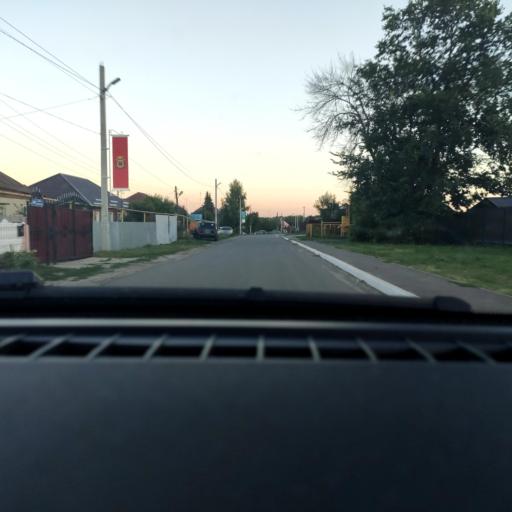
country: RU
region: Voronezj
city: Novaya Usman'
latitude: 51.6629
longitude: 39.3426
